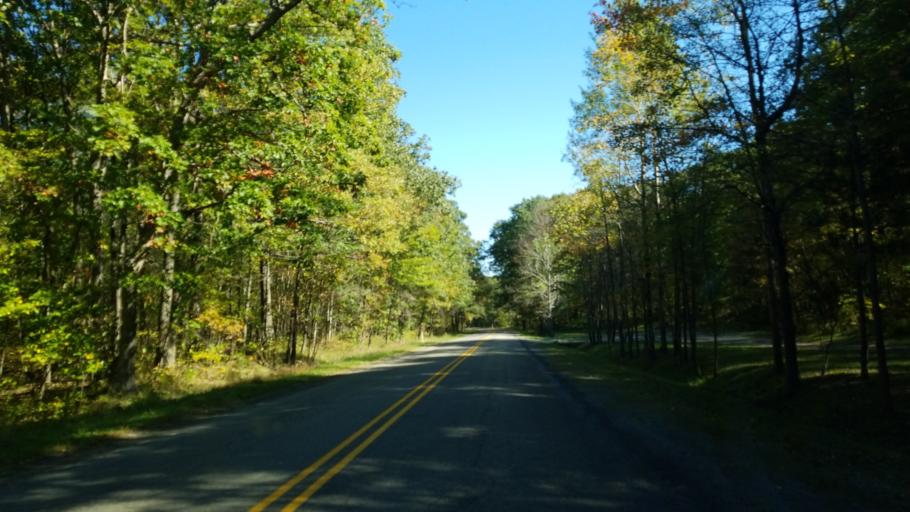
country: US
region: Pennsylvania
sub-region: Clearfield County
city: Shiloh
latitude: 41.2520
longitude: -78.3522
